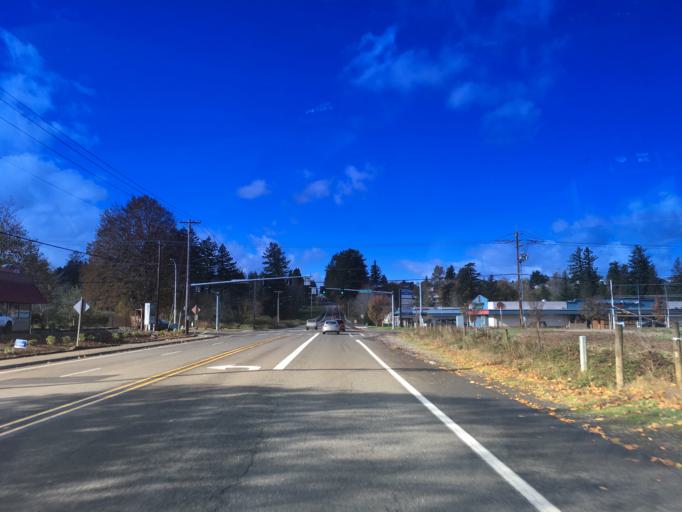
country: US
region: Oregon
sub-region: Multnomah County
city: Troutdale
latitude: 45.5190
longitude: -122.3856
